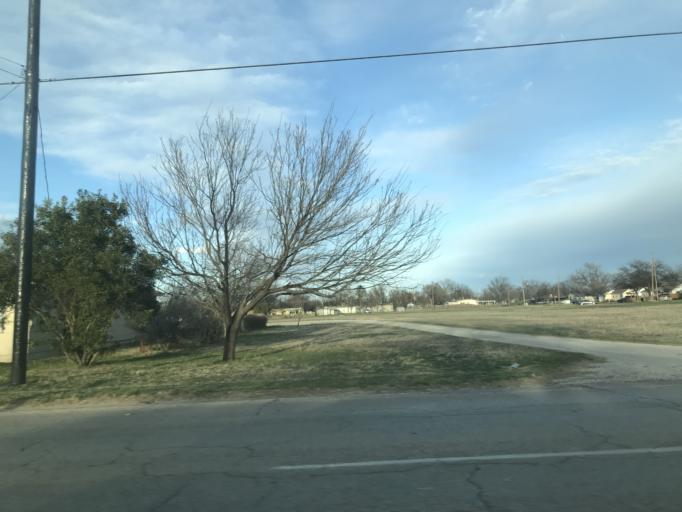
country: US
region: Texas
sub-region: Tom Green County
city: San Angelo
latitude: 31.4934
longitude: -100.4568
